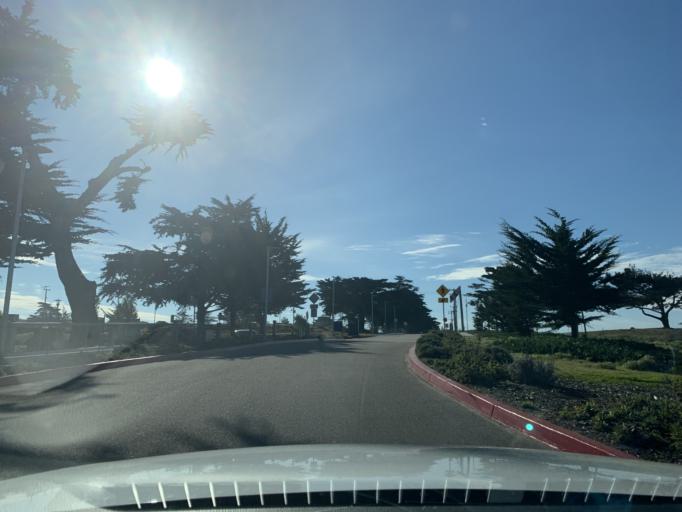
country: US
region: California
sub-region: Monterey County
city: Marina
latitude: 36.6624
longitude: -121.8144
